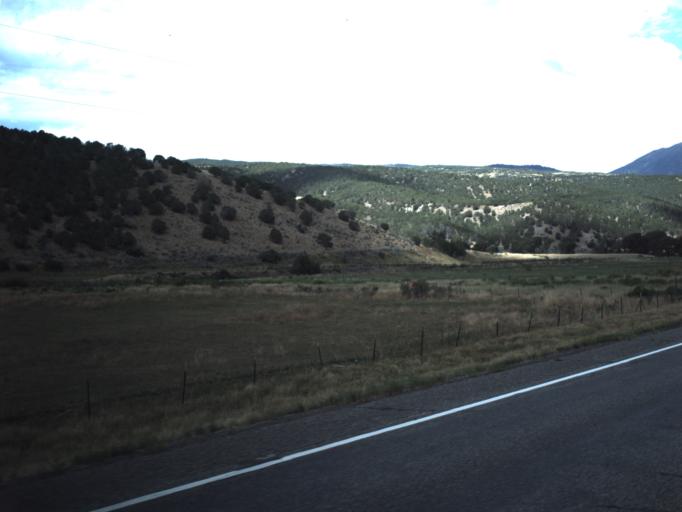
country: US
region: Utah
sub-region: Utah County
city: Woodland Hills
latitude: 39.8823
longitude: -111.5448
